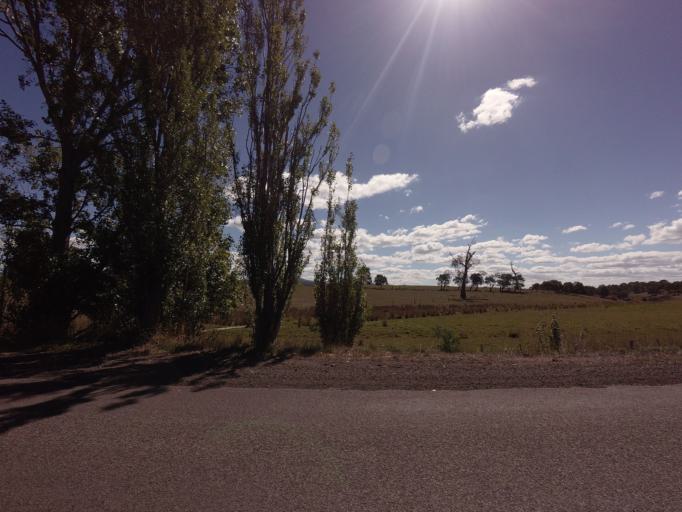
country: AU
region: Tasmania
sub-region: Break O'Day
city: St Helens
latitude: -41.6282
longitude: 147.9894
